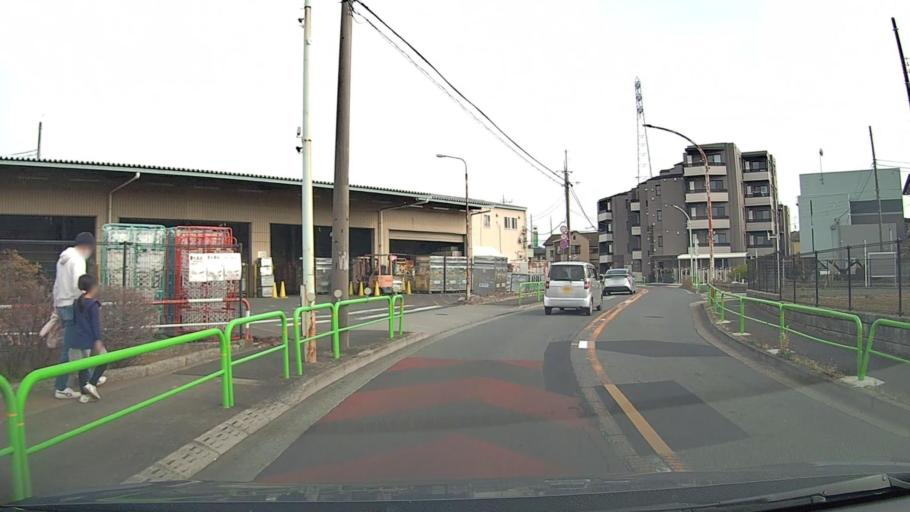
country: JP
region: Tokyo
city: Tanashicho
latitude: 35.7627
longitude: 139.5724
